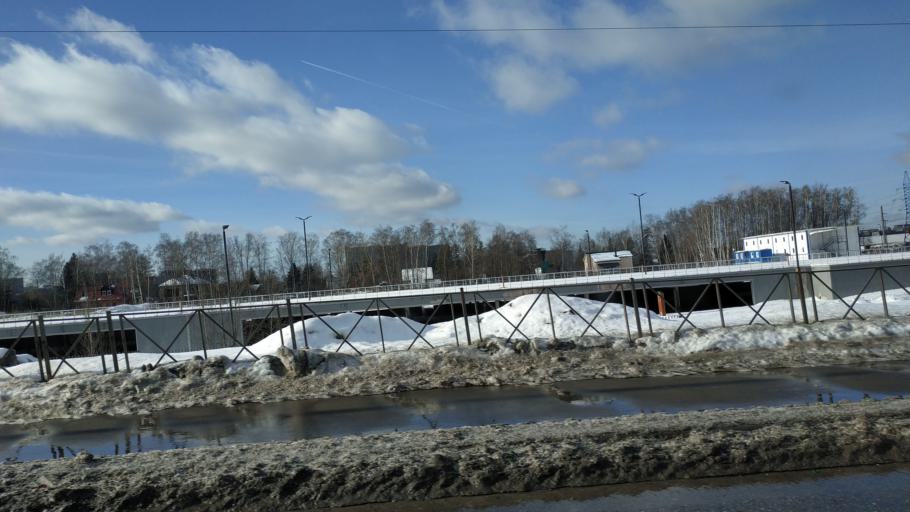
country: RU
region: Moskovskaya
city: Kommunarka
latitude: 55.5939
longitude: 37.4775
